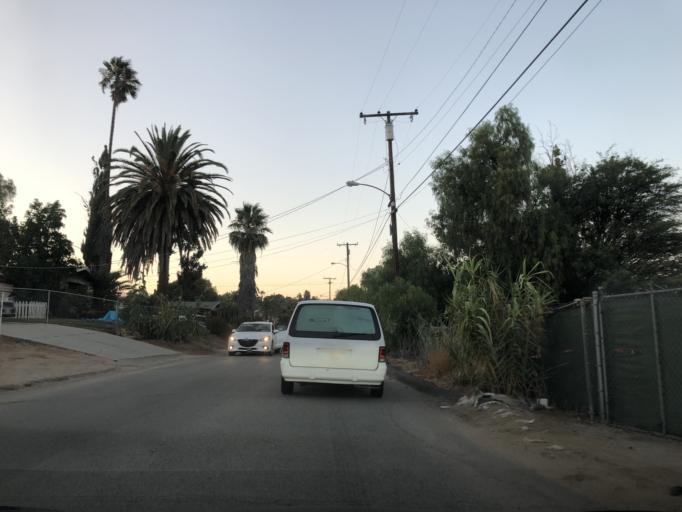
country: US
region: California
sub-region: Riverside County
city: Pedley
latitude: 33.9453
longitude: -117.4958
